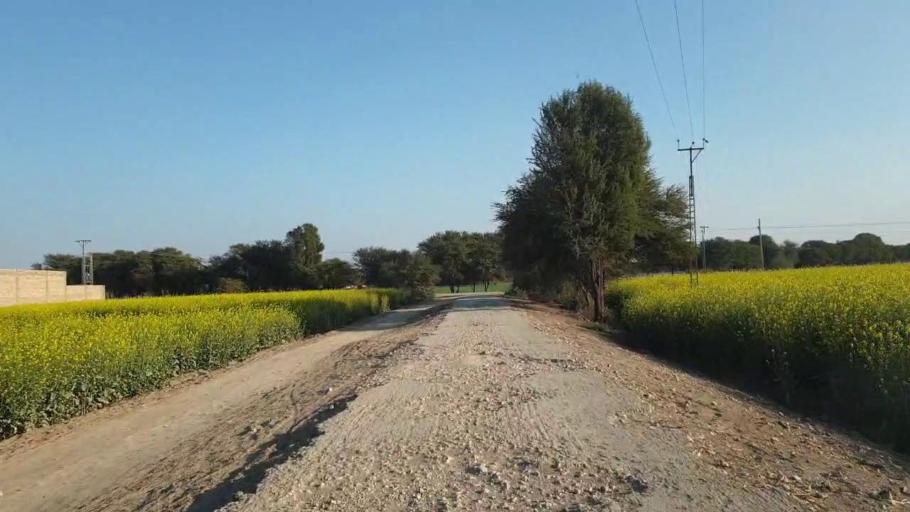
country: PK
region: Sindh
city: Shahpur Chakar
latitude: 26.1258
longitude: 68.5594
